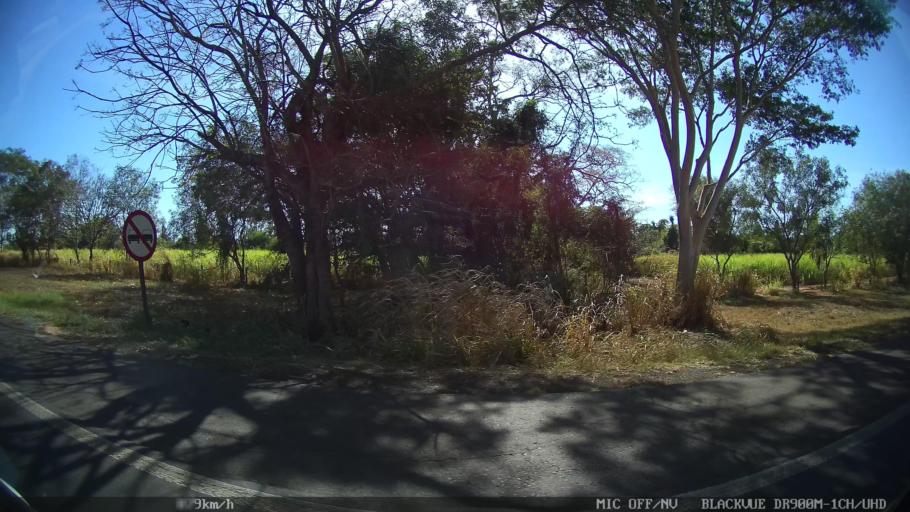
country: BR
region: Sao Paulo
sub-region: Barretos
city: Barretos
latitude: -20.5740
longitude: -48.6771
